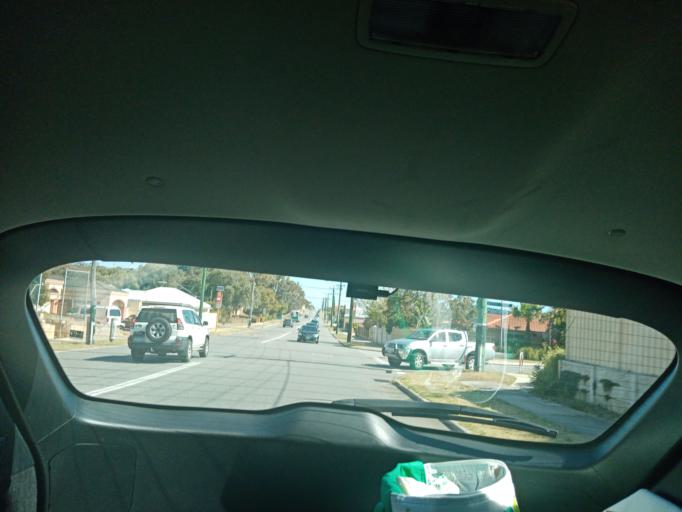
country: AU
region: Western Australia
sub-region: City of Cockburn
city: Spearwood
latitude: -32.1070
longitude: 115.7827
